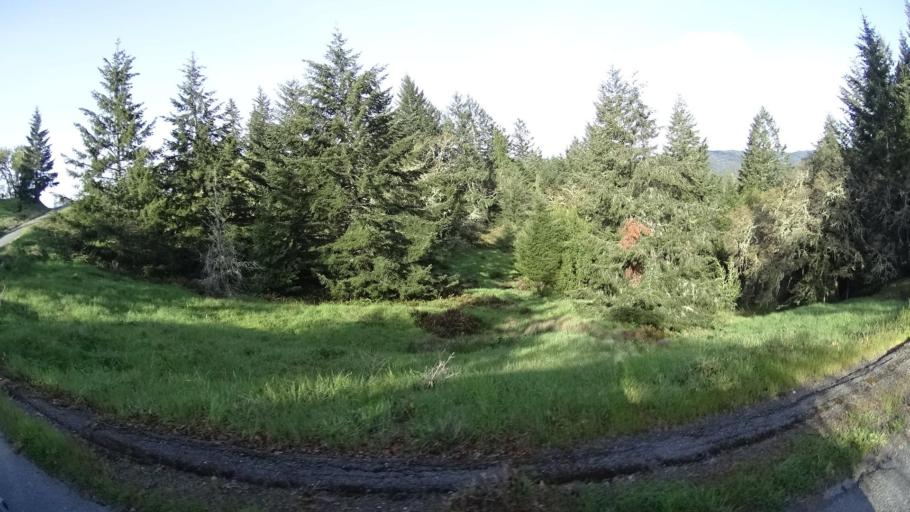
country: US
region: California
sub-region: Humboldt County
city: Hydesville
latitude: 40.6631
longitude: -123.9288
